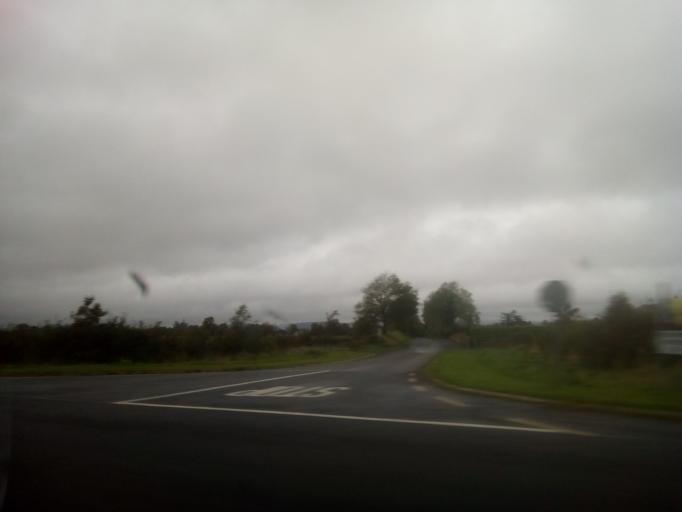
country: IE
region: Connaught
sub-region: Roscommon
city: Ballaghaderreen
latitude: 53.8857
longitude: -8.4703
